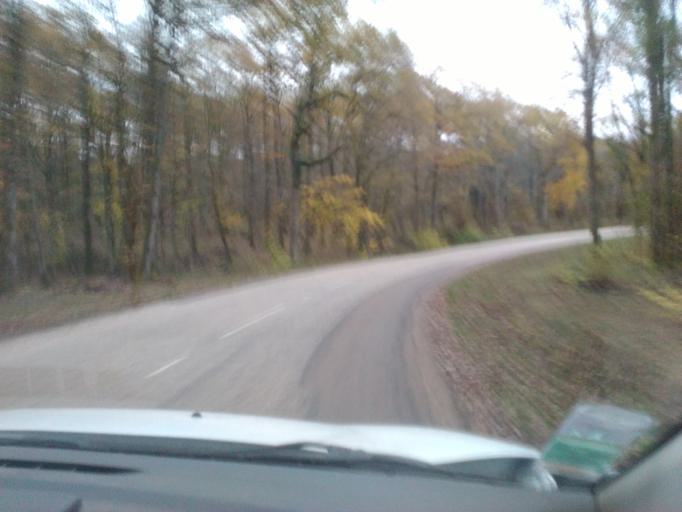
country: FR
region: Lorraine
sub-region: Departement des Vosges
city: Darnieulles
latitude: 48.2330
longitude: 6.2938
